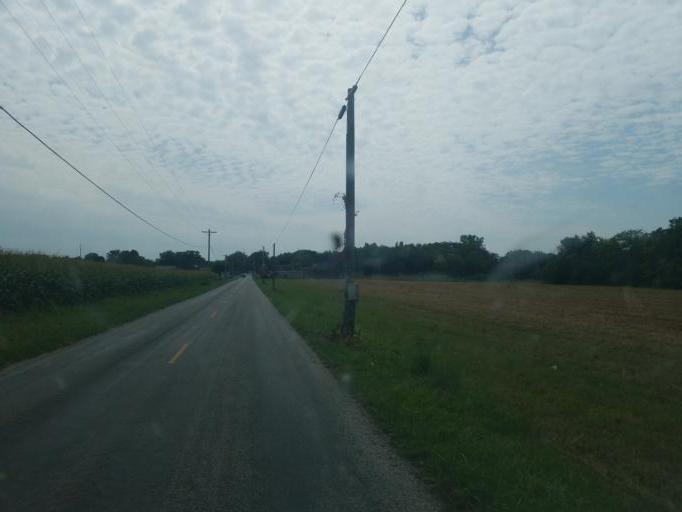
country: US
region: Ohio
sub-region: Marion County
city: Prospect
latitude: 40.5365
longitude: -83.2134
